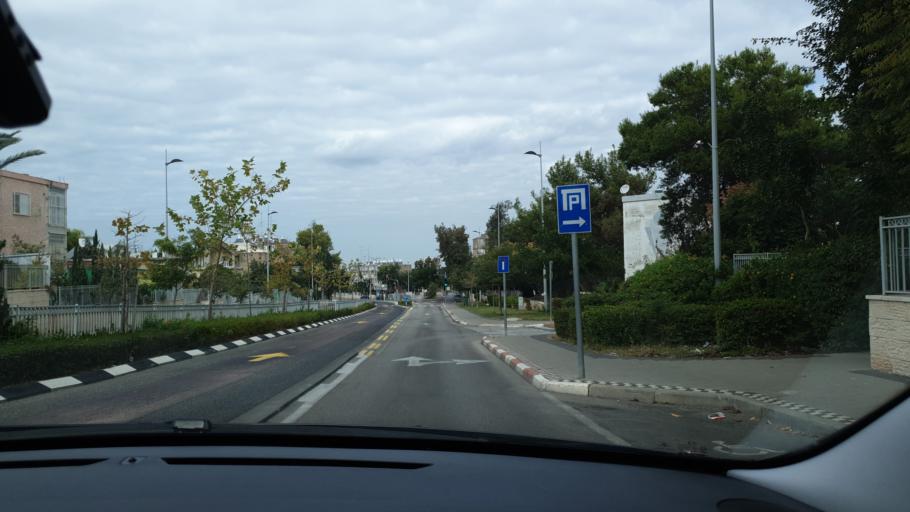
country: IL
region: Haifa
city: Qiryat Ata
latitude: 32.8115
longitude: 35.1147
